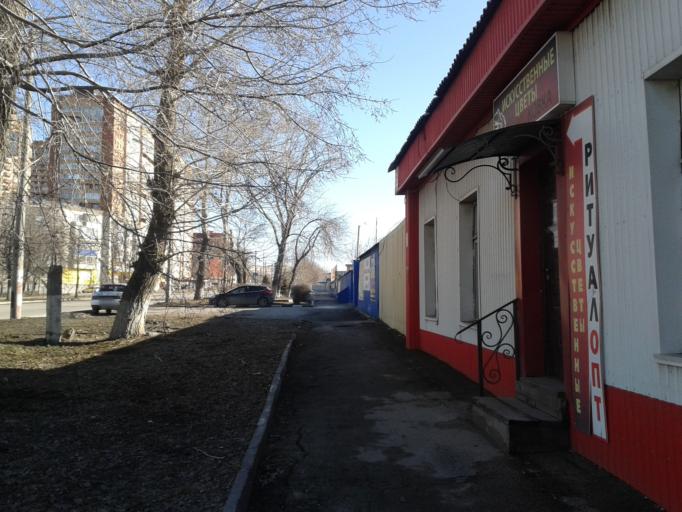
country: RU
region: Ulyanovsk
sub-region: Ulyanovskiy Rayon
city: Ulyanovsk
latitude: 54.2987
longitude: 48.3808
